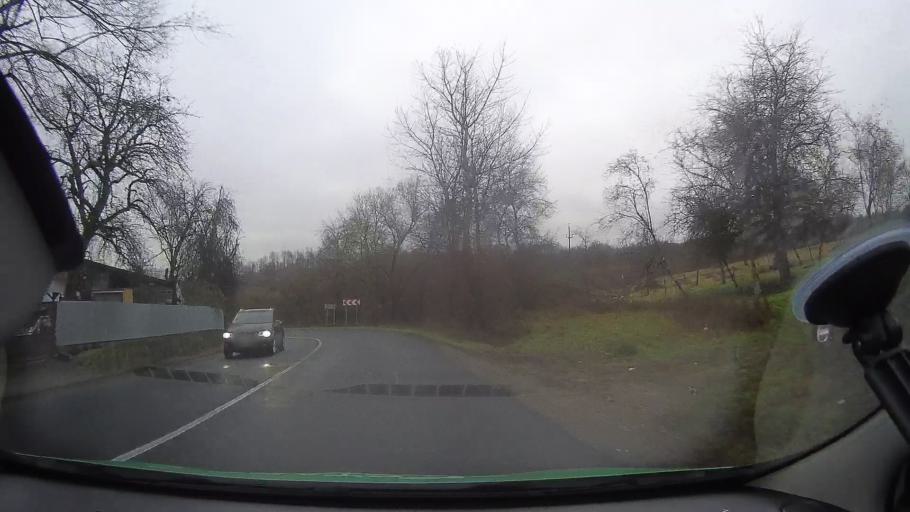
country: RO
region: Arad
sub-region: Comuna Varfurile
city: Varfurile
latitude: 46.3219
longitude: 22.4965
